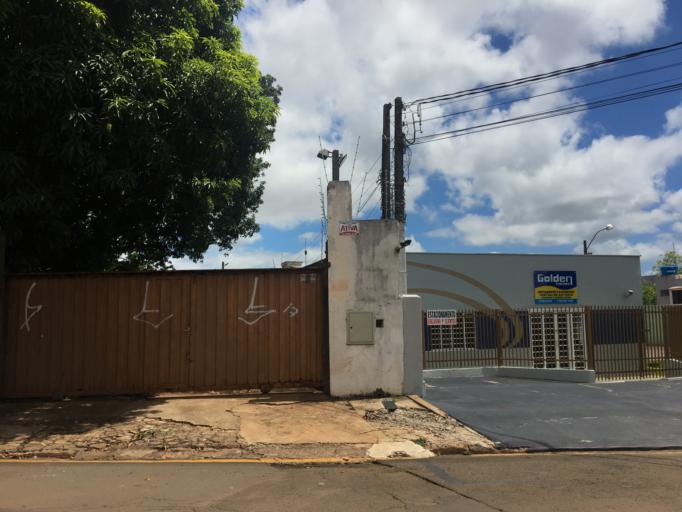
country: BR
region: Parana
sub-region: Londrina
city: Londrina
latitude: -23.2955
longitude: -51.1666
